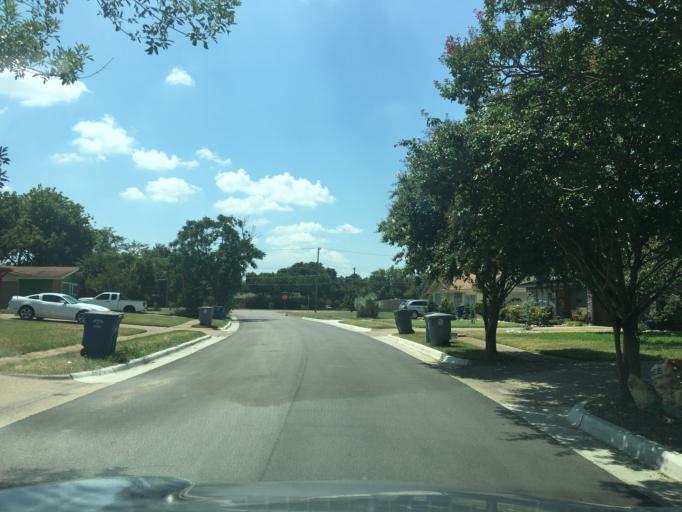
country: US
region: Texas
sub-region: Dallas County
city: Garland
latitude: 32.8653
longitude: -96.6889
